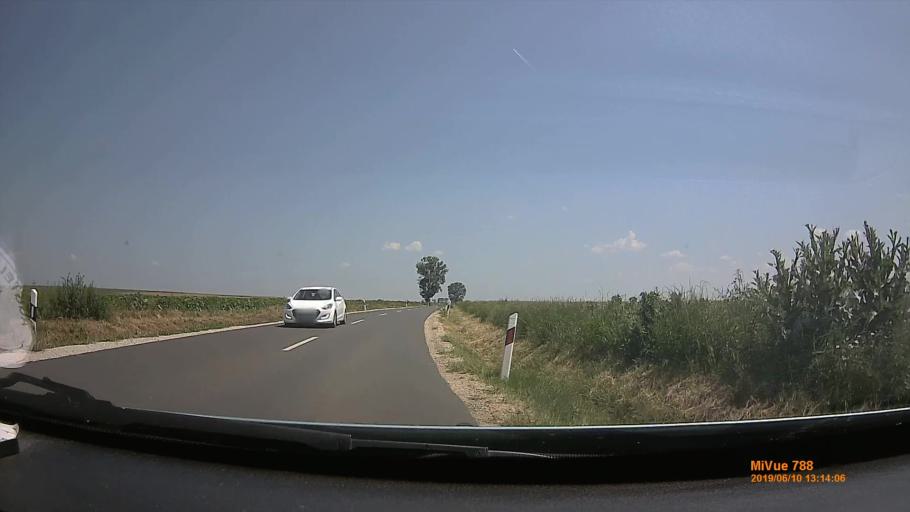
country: HU
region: Borsod-Abauj-Zemplen
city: Hernadnemeti
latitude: 48.0581
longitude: 21.0163
